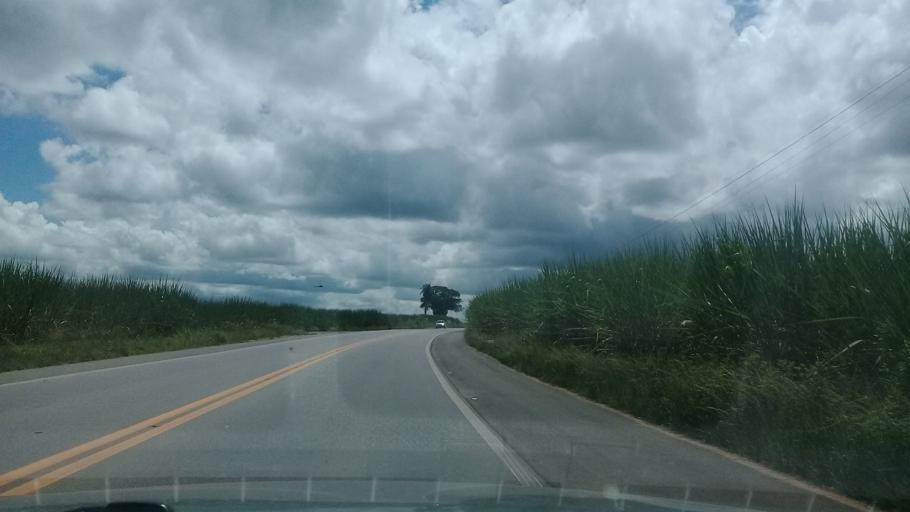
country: BR
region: Pernambuco
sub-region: Carpina
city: Carpina
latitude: -7.8175
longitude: -35.2458
